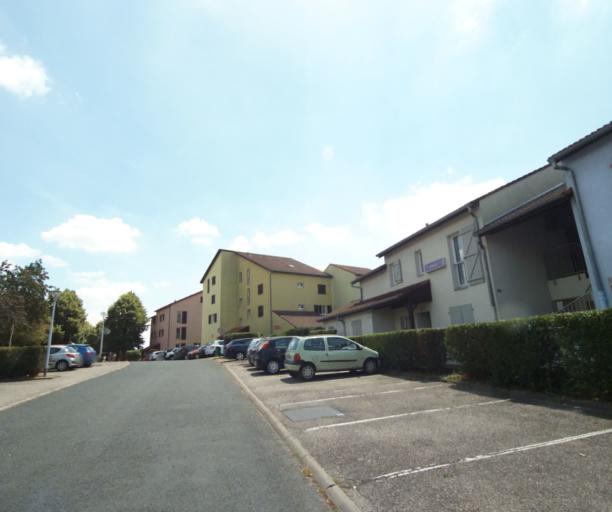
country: FR
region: Lorraine
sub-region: Departement de Meurthe-et-Moselle
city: Luneville
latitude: 48.5983
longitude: 6.4765
